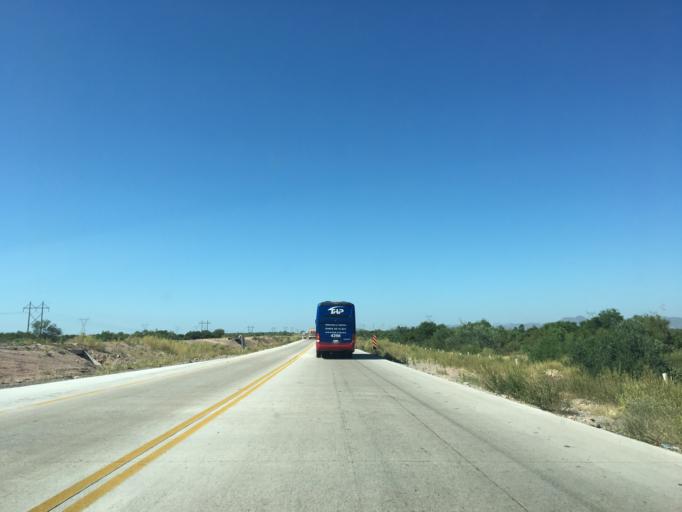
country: MX
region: Sonora
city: Heroica Guaymas
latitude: 28.0765
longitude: -110.9526
